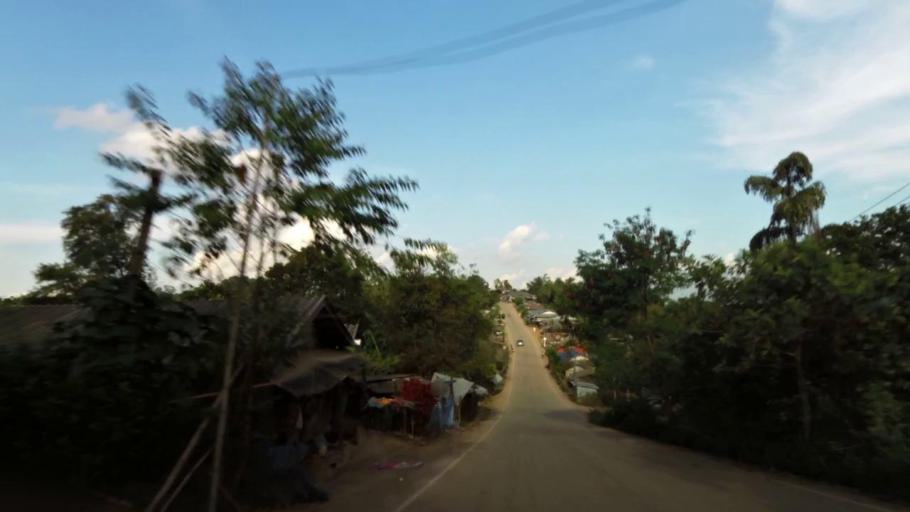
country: TH
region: Chiang Rai
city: Khun Tan
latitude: 19.8712
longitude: 100.3407
